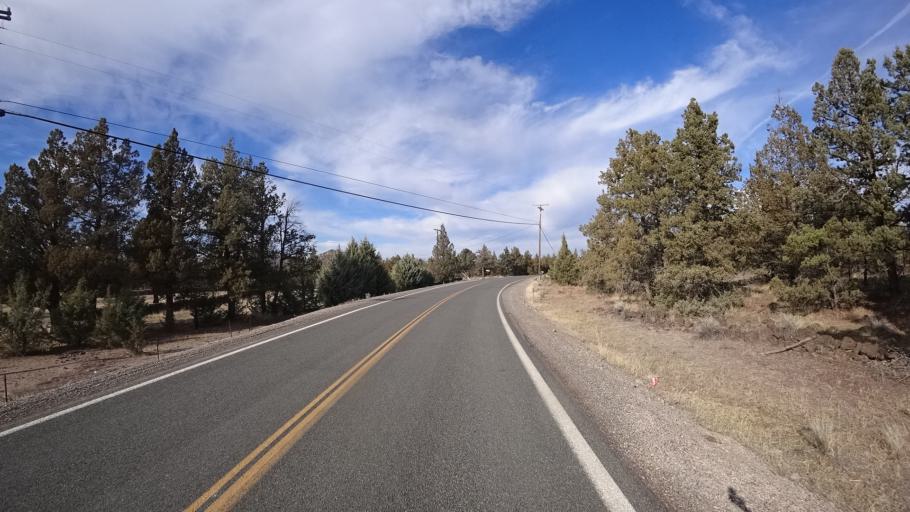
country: US
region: California
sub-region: Siskiyou County
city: Montague
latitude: 41.6484
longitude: -122.3992
